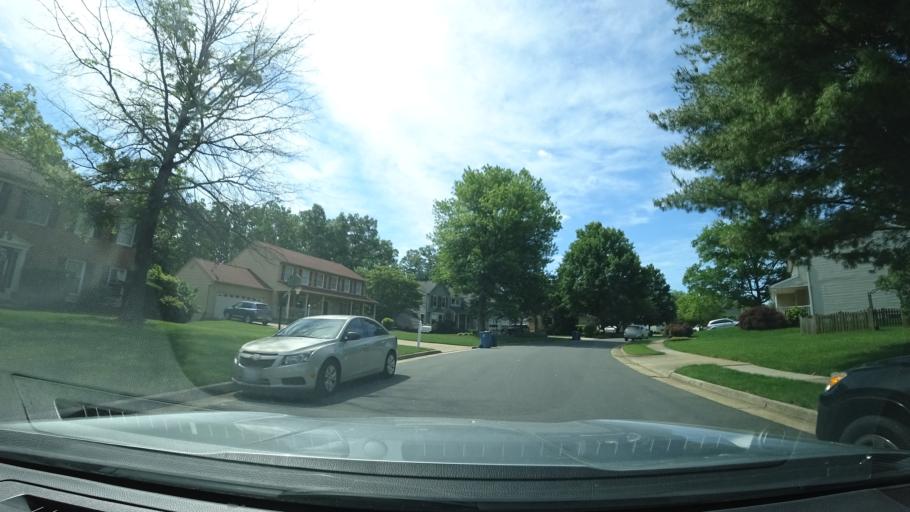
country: US
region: Virginia
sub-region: Loudoun County
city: Oak Grove
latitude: 38.9856
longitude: -77.4009
